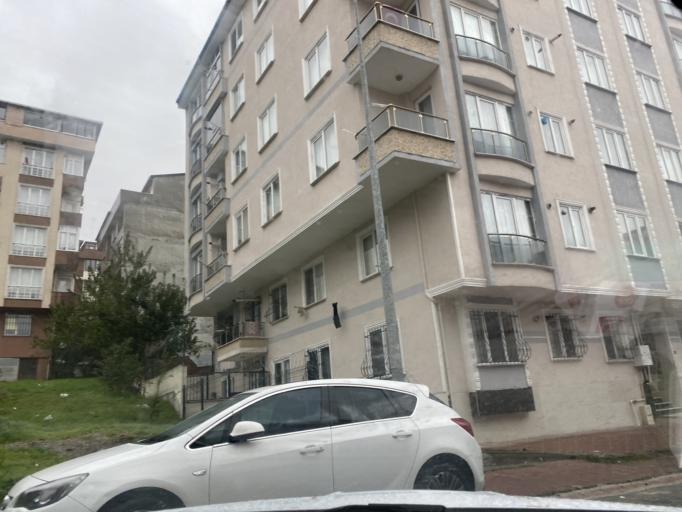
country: TR
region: Istanbul
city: Esenyurt
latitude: 41.0211
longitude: 28.6622
